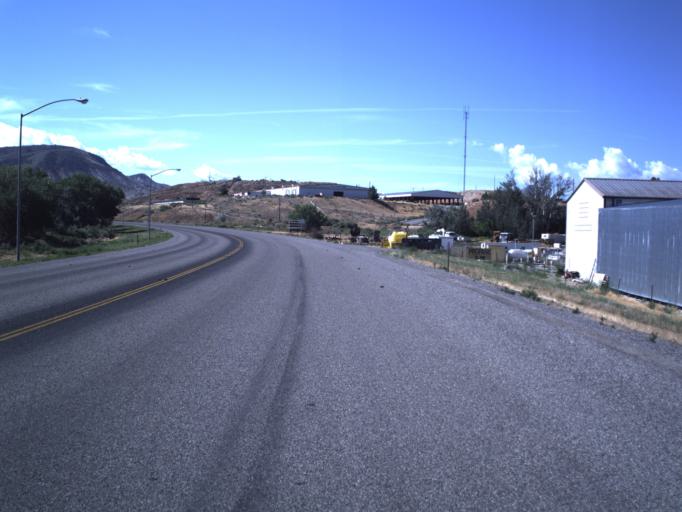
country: US
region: Utah
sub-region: Sevier County
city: Salina
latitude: 38.9522
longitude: -111.8601
